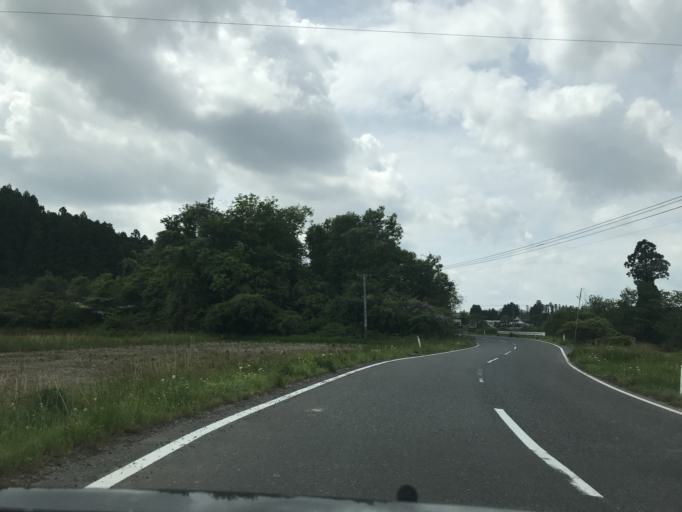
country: JP
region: Iwate
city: Ichinoseki
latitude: 38.8318
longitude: 141.0212
